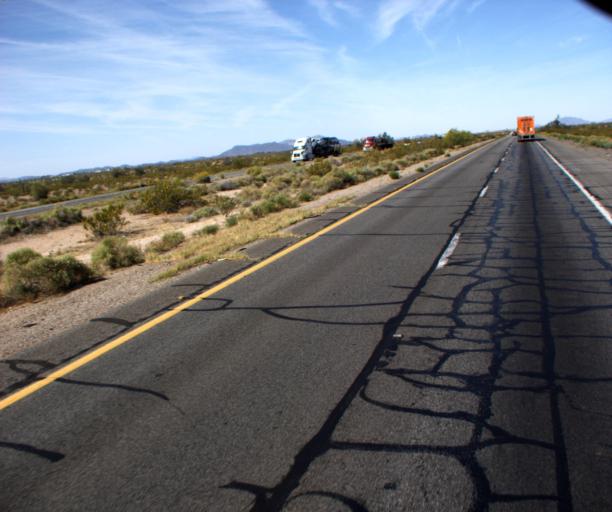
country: US
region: Arizona
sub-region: Maricopa County
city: Buckeye
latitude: 33.4549
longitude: -112.7463
